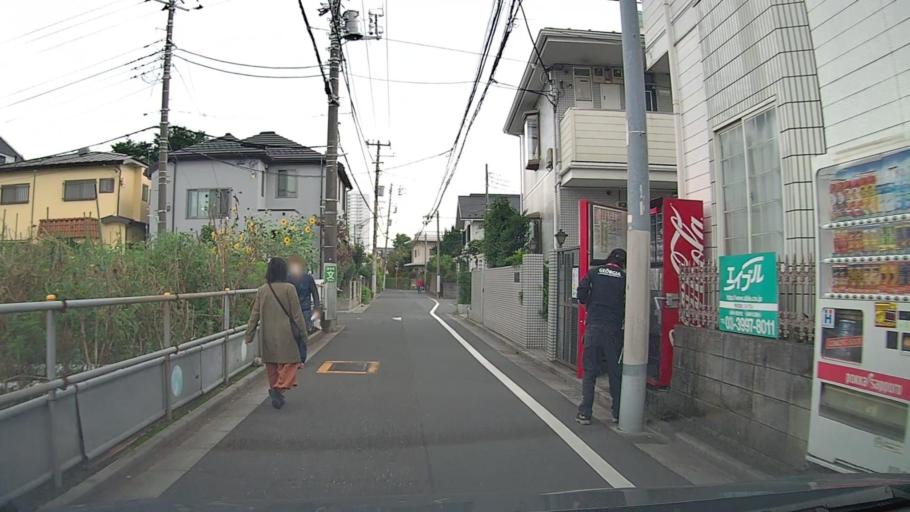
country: JP
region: Saitama
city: Wako
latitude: 35.7493
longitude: 139.6013
